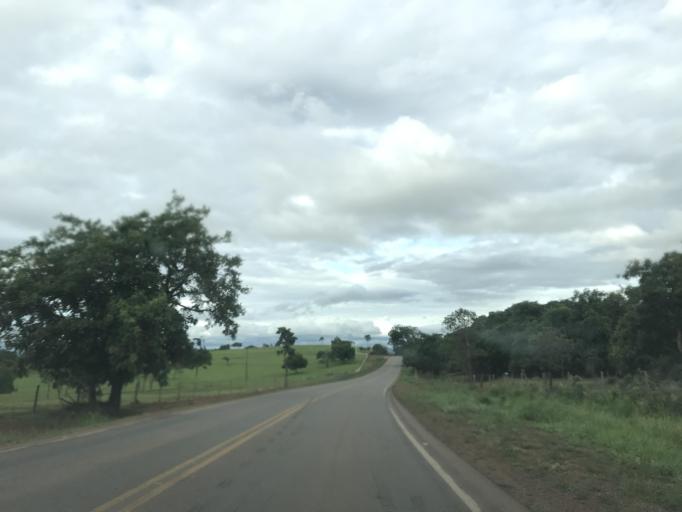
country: BR
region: Goias
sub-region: Vianopolis
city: Vianopolis
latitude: -16.7066
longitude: -48.3944
